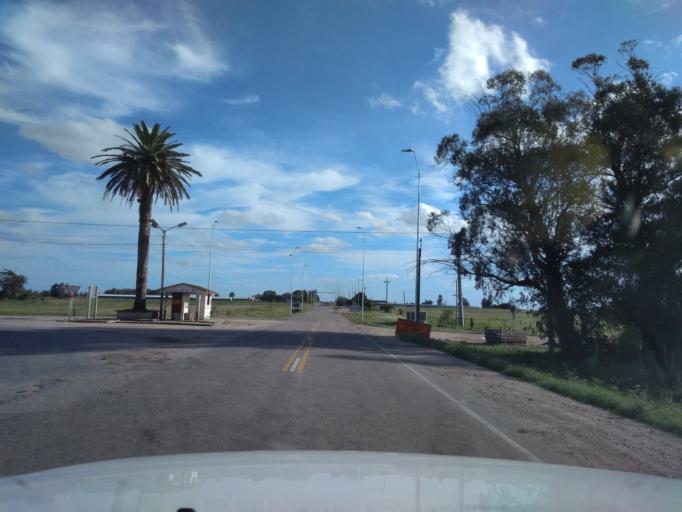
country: UY
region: Canelones
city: San Ramon
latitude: -34.2427
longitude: -55.9253
